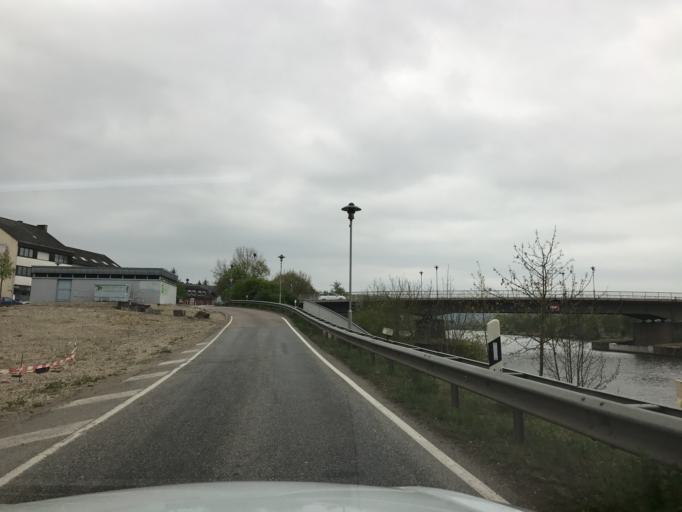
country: DE
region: Rheinland-Pfalz
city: Konz
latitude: 49.6990
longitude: 6.5704
